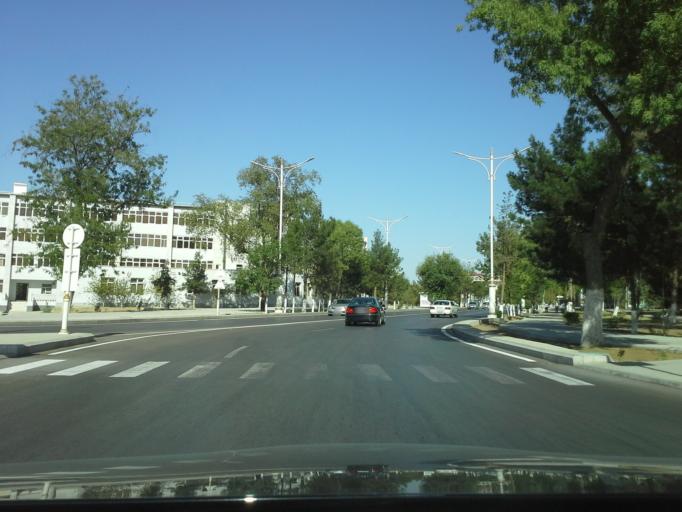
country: TM
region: Ahal
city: Ashgabat
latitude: 37.9581
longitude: 58.3459
